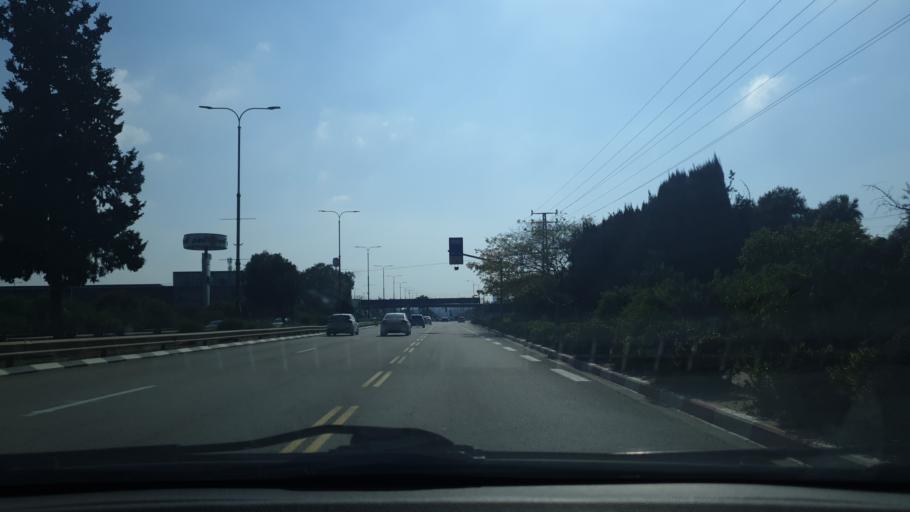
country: IL
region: Central District
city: Bet Dagan
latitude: 31.9866
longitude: 34.8111
